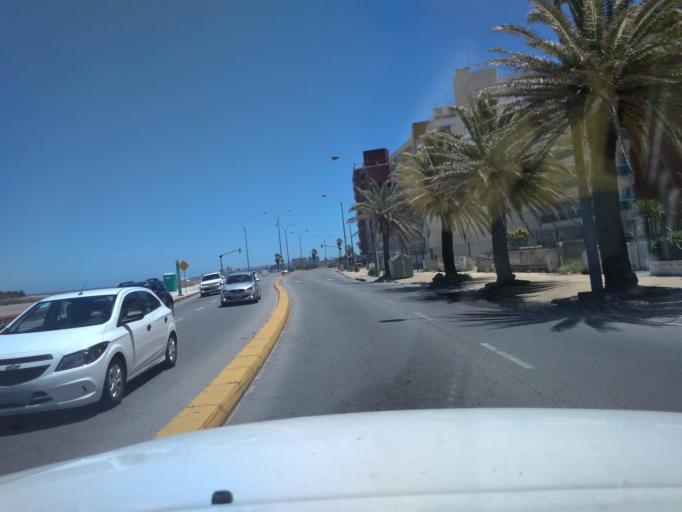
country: UY
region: Canelones
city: Paso de Carrasco
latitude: -34.8968
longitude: -56.0984
